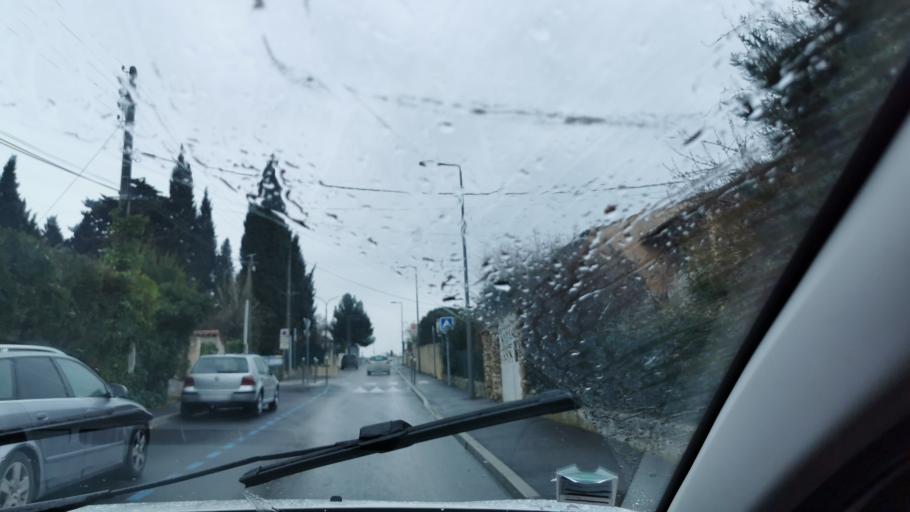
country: FR
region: Provence-Alpes-Cote d'Azur
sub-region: Departement des Bouches-du-Rhone
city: Lambesc
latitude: 43.6528
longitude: 5.2655
